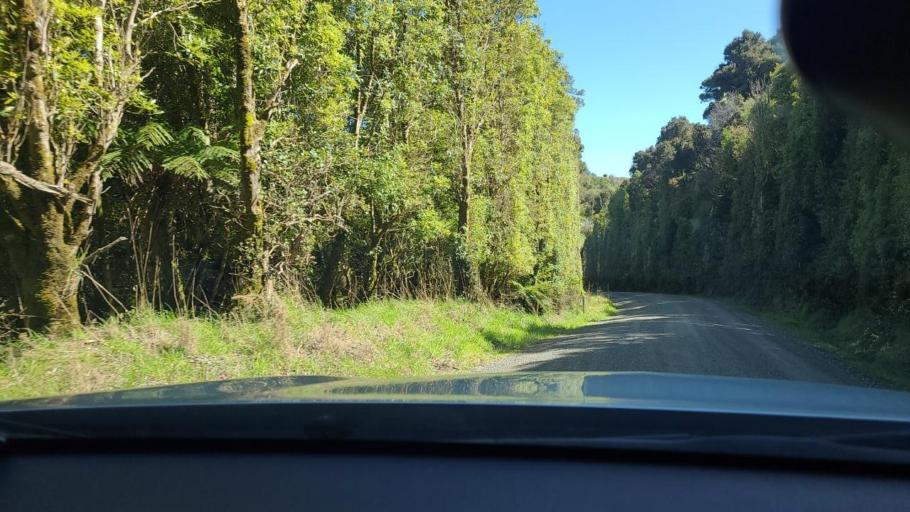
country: NZ
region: Otago
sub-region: Clutha District
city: Papatowai
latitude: -46.4842
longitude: 169.1518
